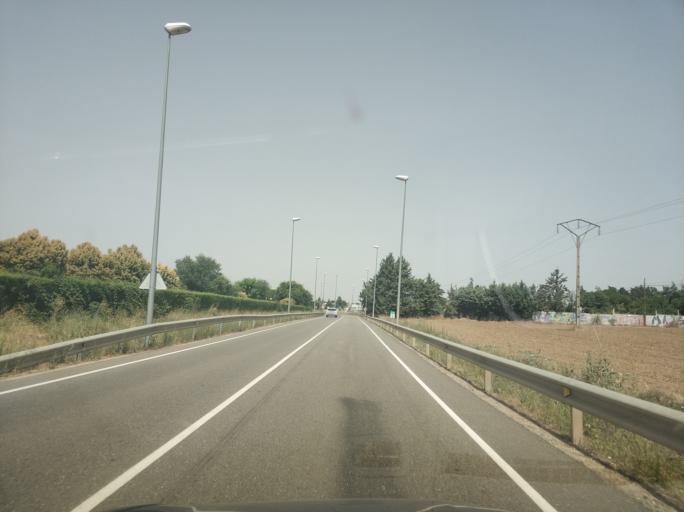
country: ES
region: Castille and Leon
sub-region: Provincia de Salamanca
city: Villamayor
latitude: 41.0077
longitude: -5.7055
